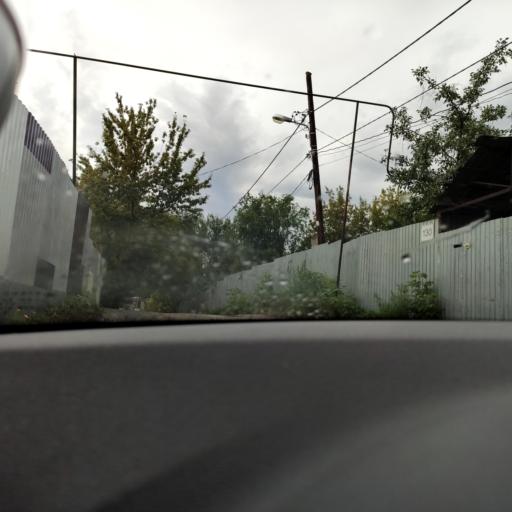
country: RU
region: Samara
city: Samara
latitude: 53.1739
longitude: 50.1574
